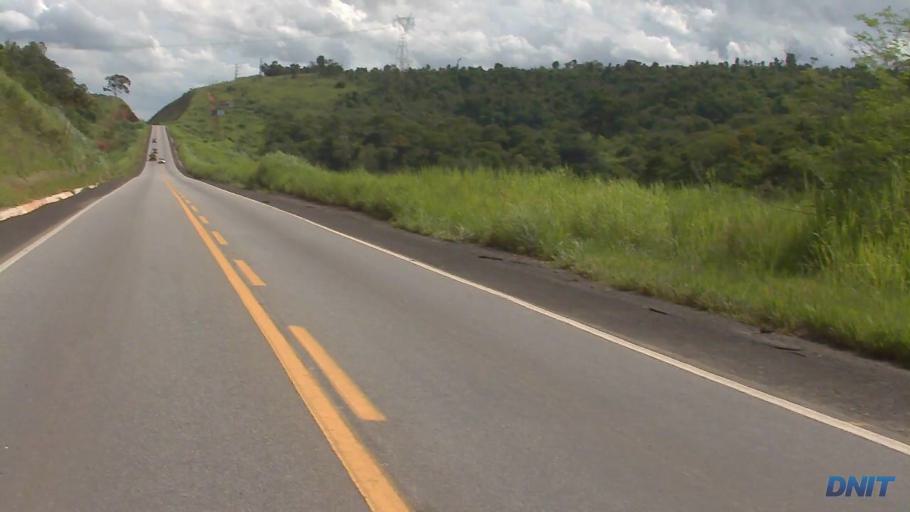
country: BR
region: Minas Gerais
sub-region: Ipaba
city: Ipaba
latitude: -19.4120
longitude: -42.4898
